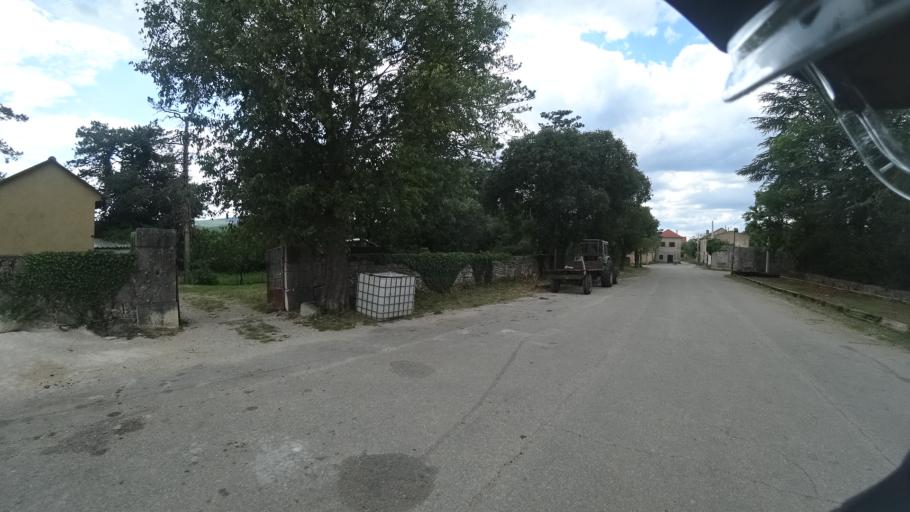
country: HR
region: Sibensko-Kniniska
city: Kistanje
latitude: 44.1078
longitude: 15.9412
